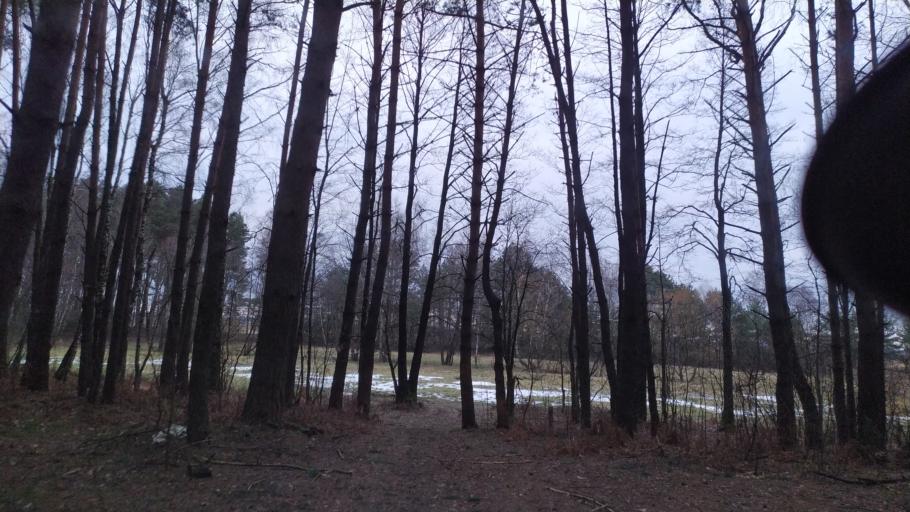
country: PL
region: Lublin Voivodeship
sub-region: Powiat lubartowski
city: Abramow
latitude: 51.4283
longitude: 22.2928
